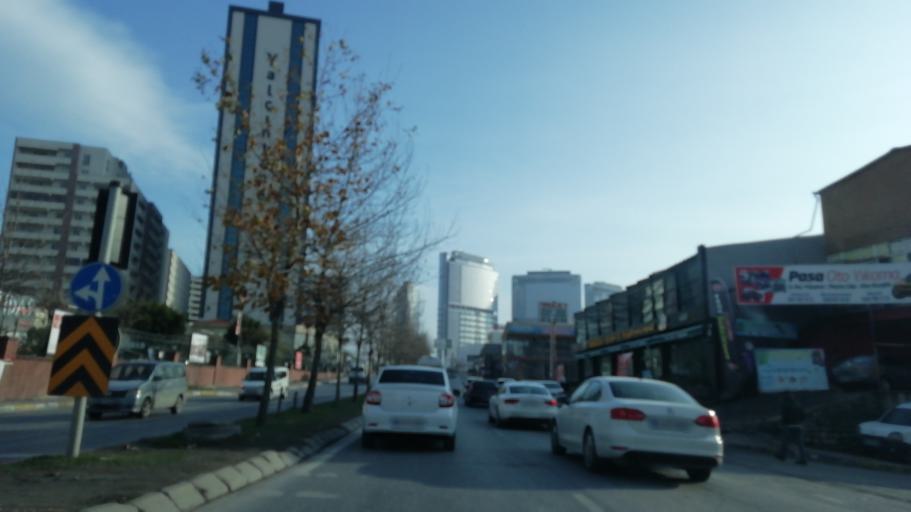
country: TR
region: Istanbul
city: Esenyurt
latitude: 41.0686
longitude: 28.6612
